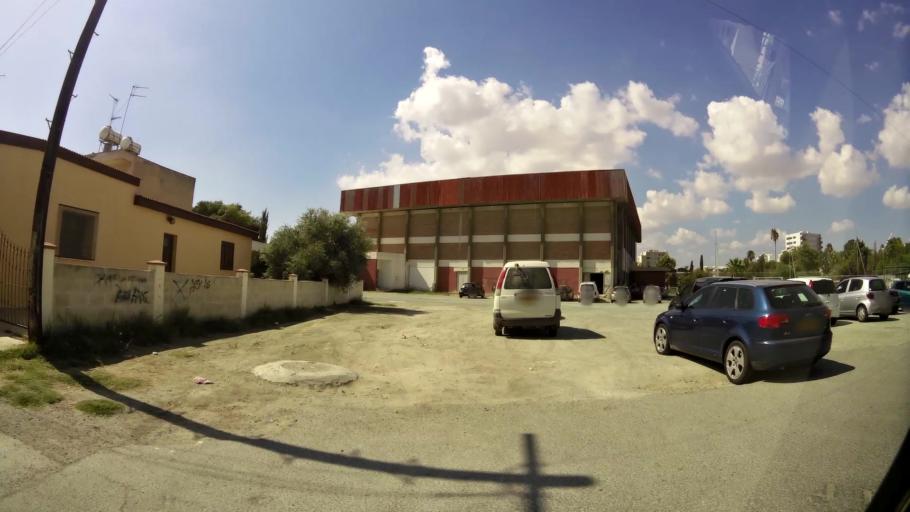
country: CY
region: Larnaka
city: Larnaca
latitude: 34.9119
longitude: 33.6325
